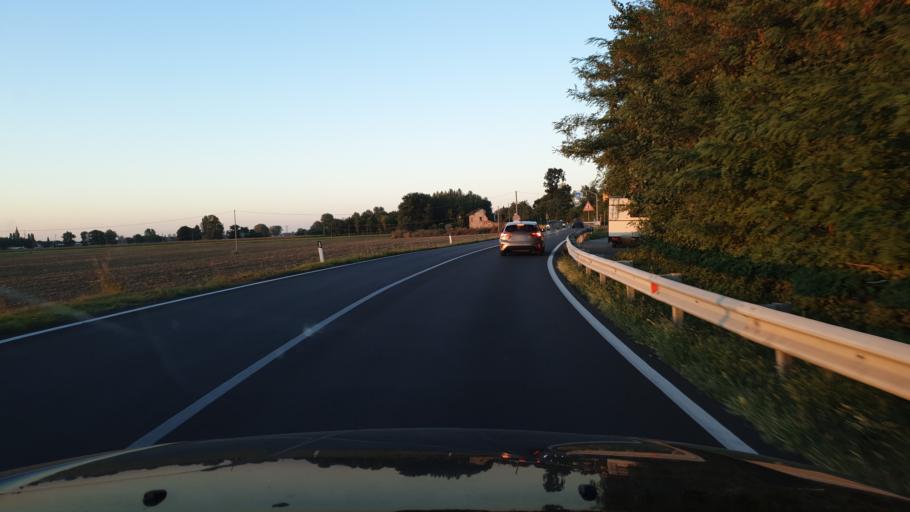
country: IT
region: Emilia-Romagna
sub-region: Provincia di Bologna
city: Progresso
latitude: 44.5589
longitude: 11.3929
